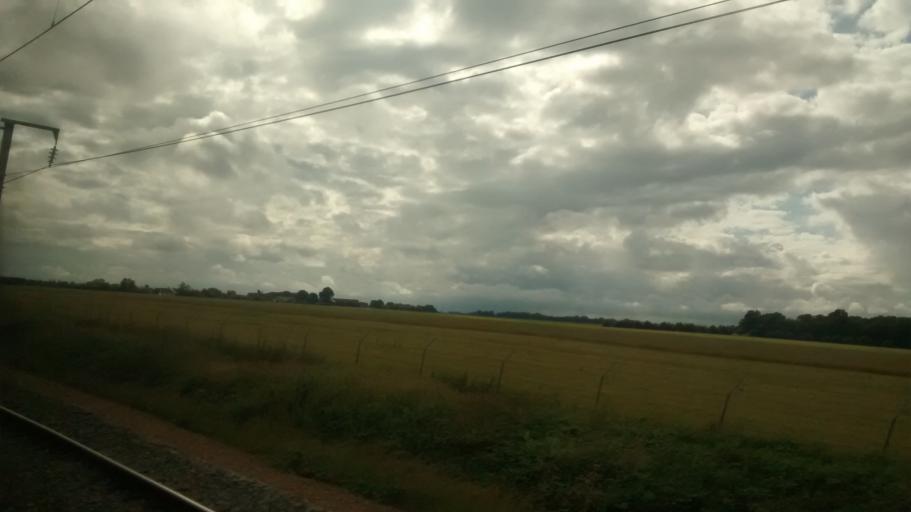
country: FR
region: Centre
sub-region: Departement d'Eure-et-Loir
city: Yevres
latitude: 48.1495
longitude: 1.2245
